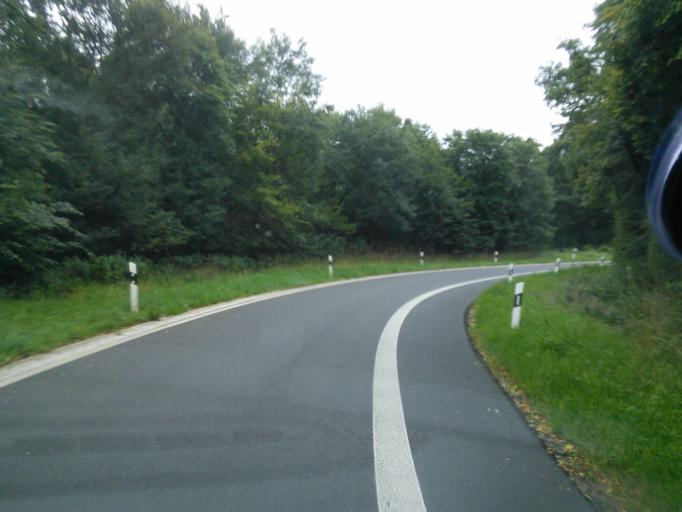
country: DE
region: North Rhine-Westphalia
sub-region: Regierungsbezirk Koln
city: Bonn
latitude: 50.7508
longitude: 7.1413
